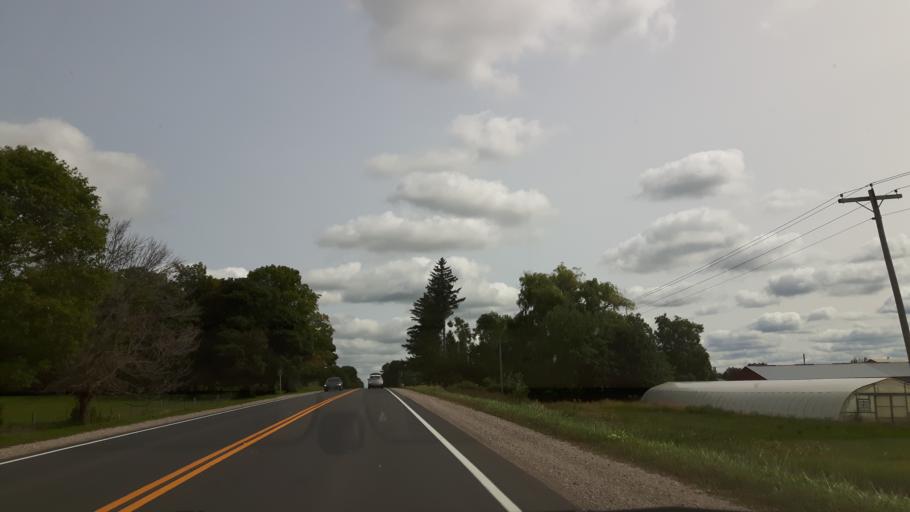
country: CA
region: Ontario
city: Bluewater
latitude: 43.5983
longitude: -81.4966
